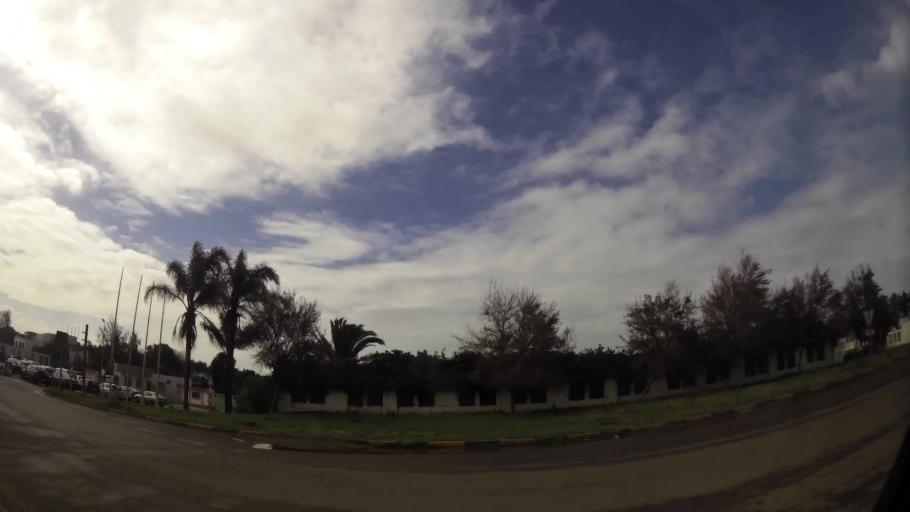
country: MA
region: Grand Casablanca
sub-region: Mohammedia
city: Mohammedia
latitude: 33.6376
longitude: -7.4438
